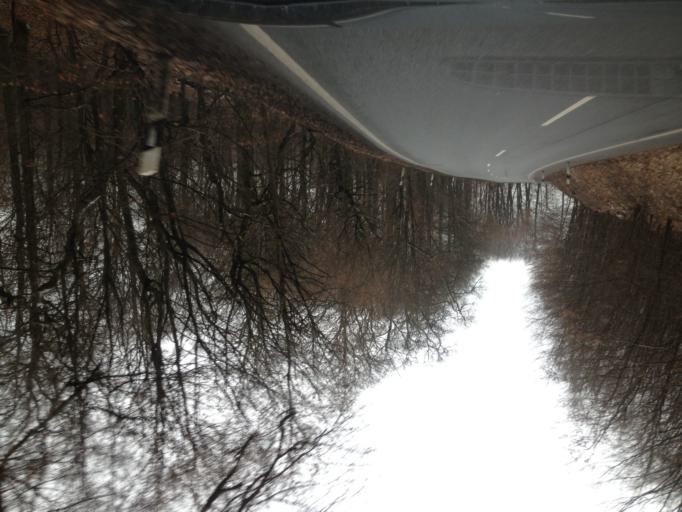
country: DE
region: Saarland
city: Hangard
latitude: 49.3995
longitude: 7.2414
